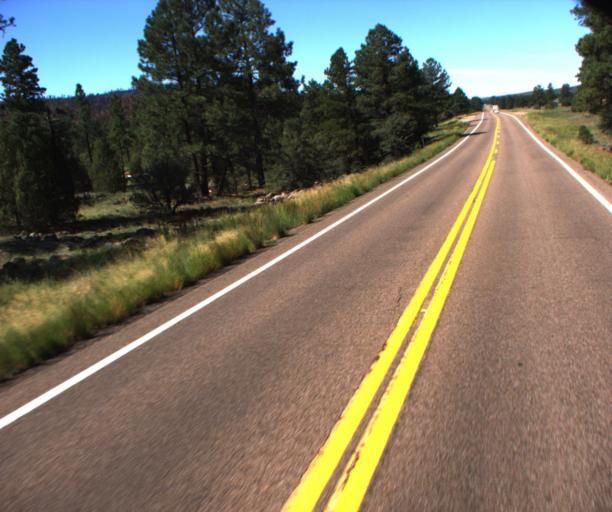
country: US
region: Arizona
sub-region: Navajo County
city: Lake of the Woods
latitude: 34.1117
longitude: -110.1452
